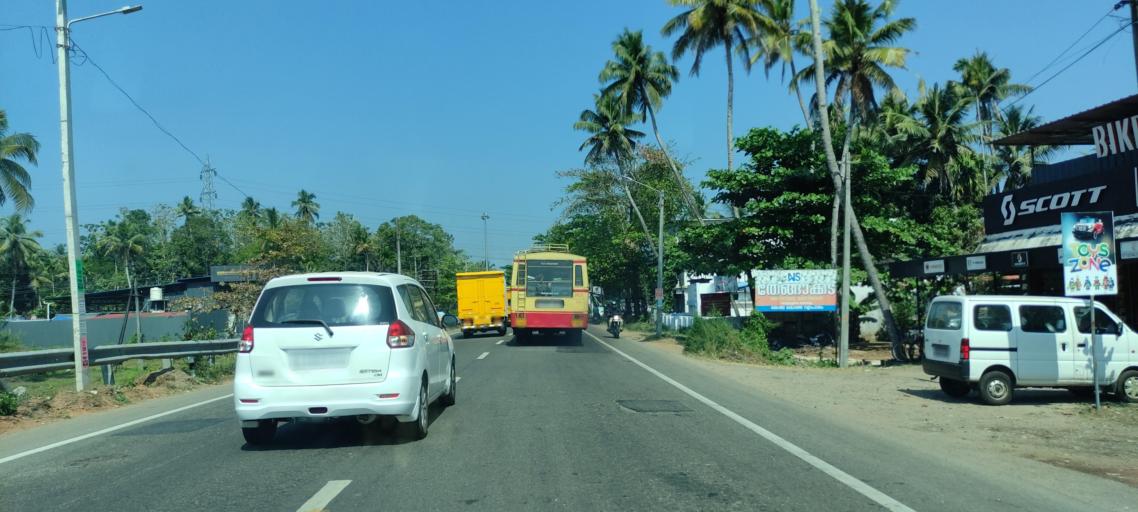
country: IN
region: Kerala
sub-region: Alappuzha
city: Kayankulam
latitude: 9.1899
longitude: 76.4874
